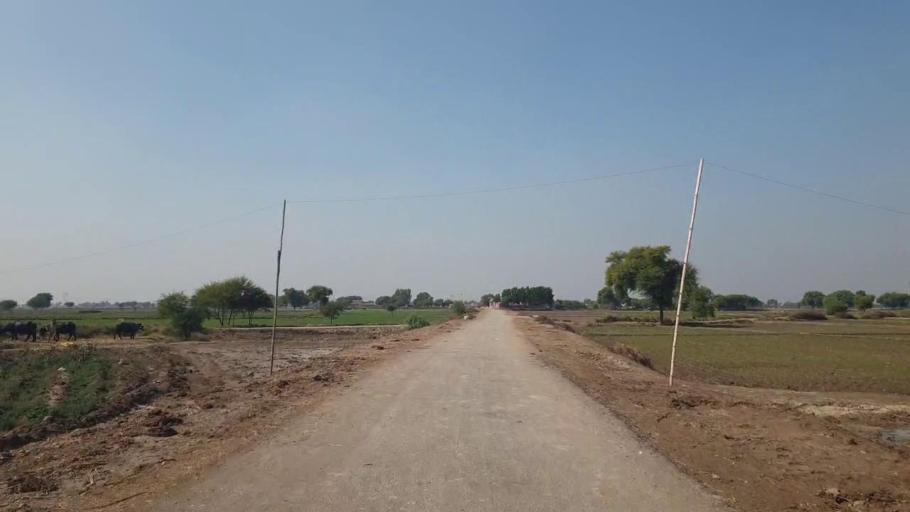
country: PK
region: Sindh
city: Sehwan
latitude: 26.4281
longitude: 67.8219
